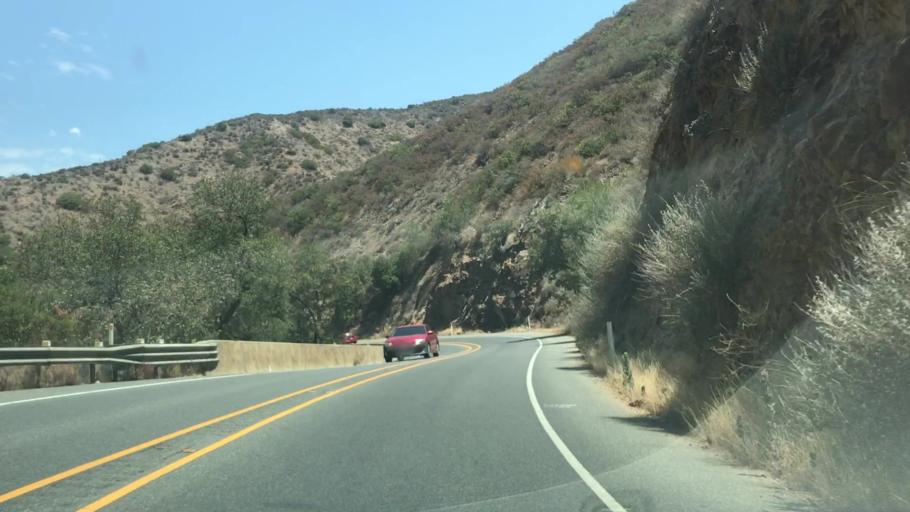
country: US
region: California
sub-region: Orange County
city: Coto De Caza
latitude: 33.5941
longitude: -117.4868
